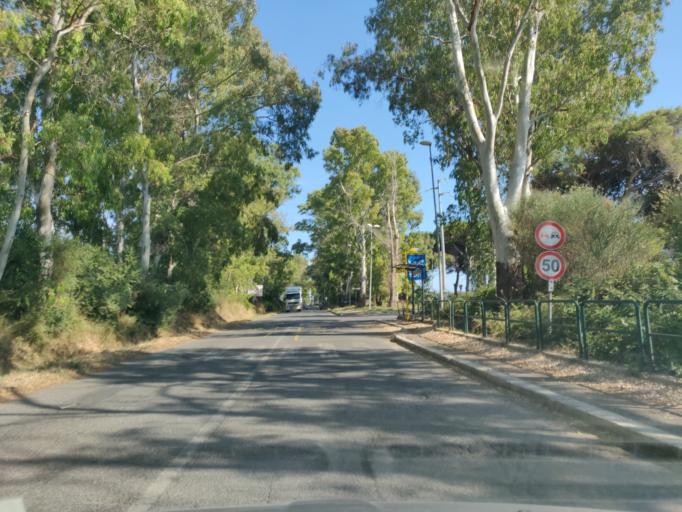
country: IT
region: Latium
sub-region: Citta metropolitana di Roma Capitale
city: Aurelia
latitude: 42.1459
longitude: 11.7622
